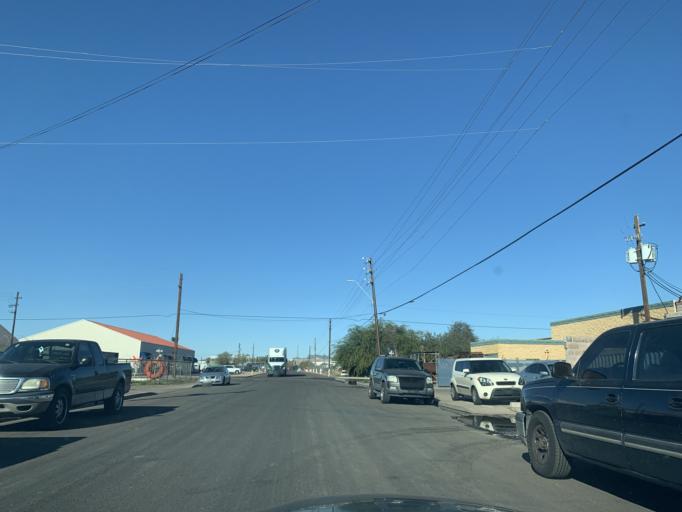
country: US
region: Arizona
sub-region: Maricopa County
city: Tempe Junction
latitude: 33.4177
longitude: -111.9997
